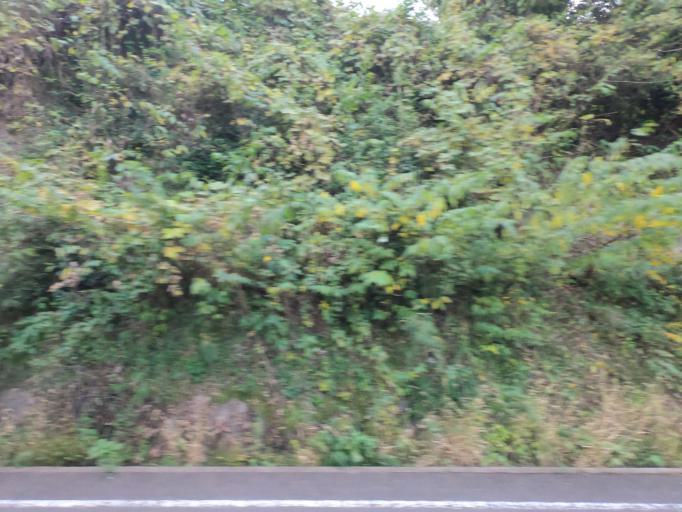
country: JP
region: Kumamoto
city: Minamata
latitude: 32.2619
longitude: 130.5083
